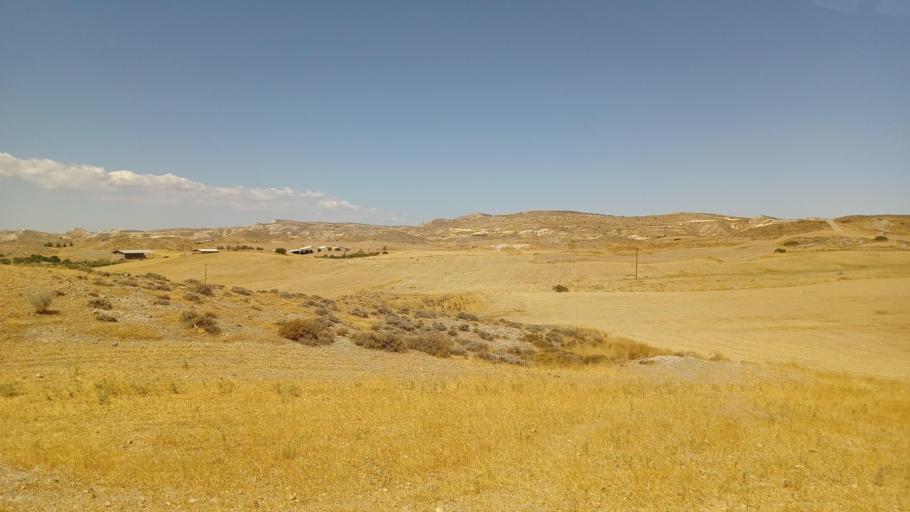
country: CY
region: Larnaka
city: Troulloi
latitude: 35.0214
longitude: 33.5974
